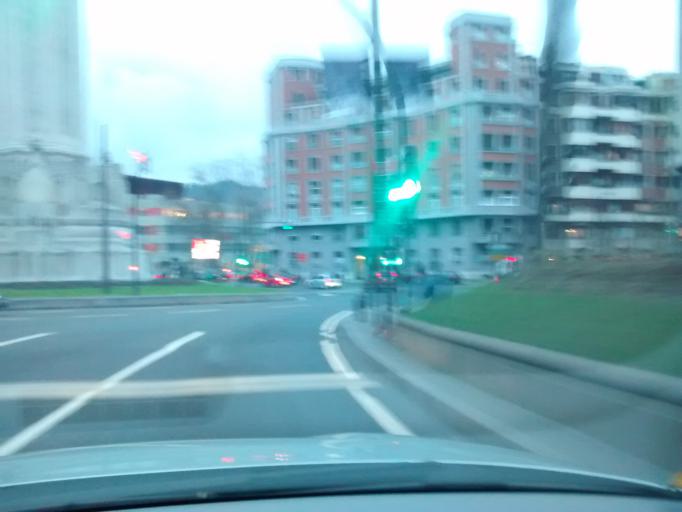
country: ES
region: Basque Country
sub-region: Bizkaia
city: Bilbao
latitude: 43.2648
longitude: -2.9455
